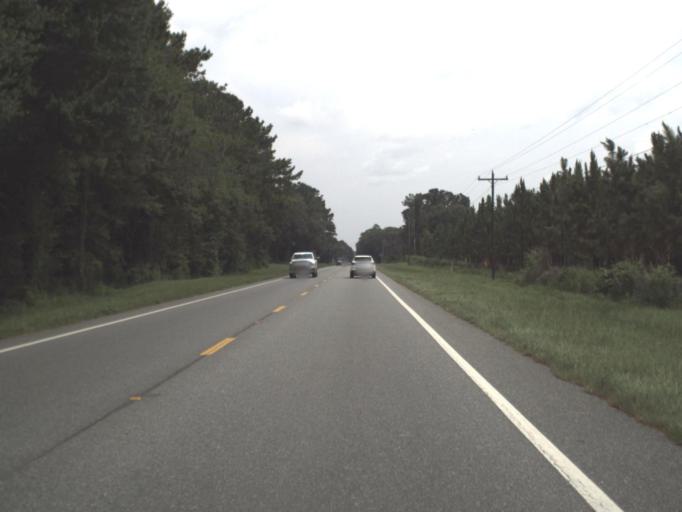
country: US
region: Florida
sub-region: Columbia County
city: Watertown
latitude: 30.0590
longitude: -82.5994
